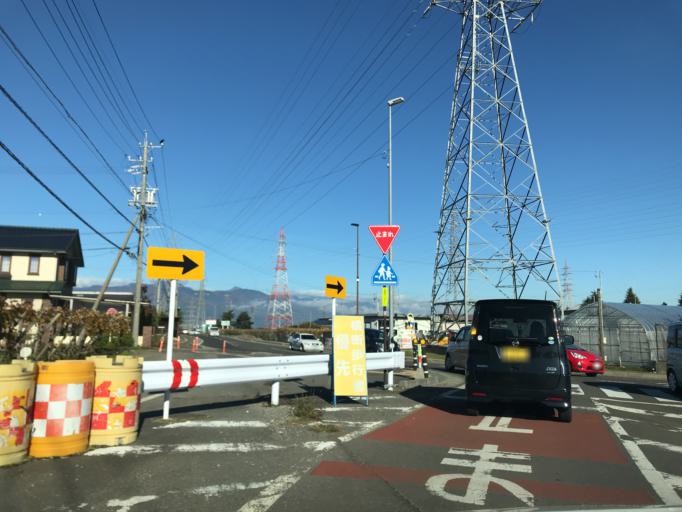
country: JP
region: Nagano
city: Shiojiri
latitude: 36.1233
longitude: 137.9393
